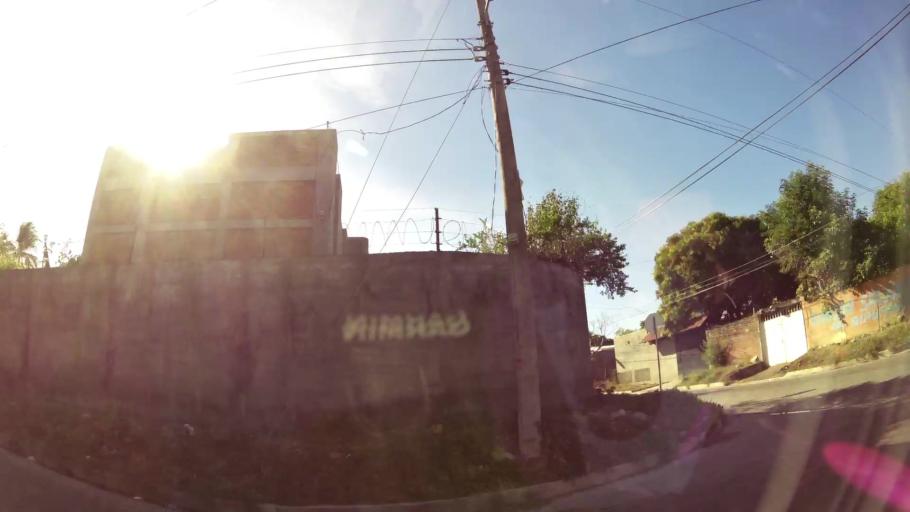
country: SV
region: San Miguel
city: San Miguel
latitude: 13.4761
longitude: -88.1938
